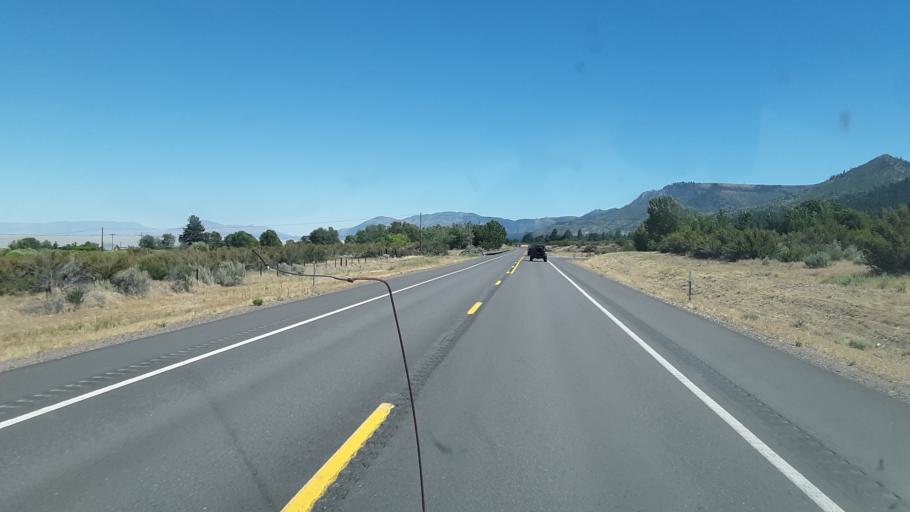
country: US
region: California
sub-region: Lassen County
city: Janesville
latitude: 40.2773
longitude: -120.4847
